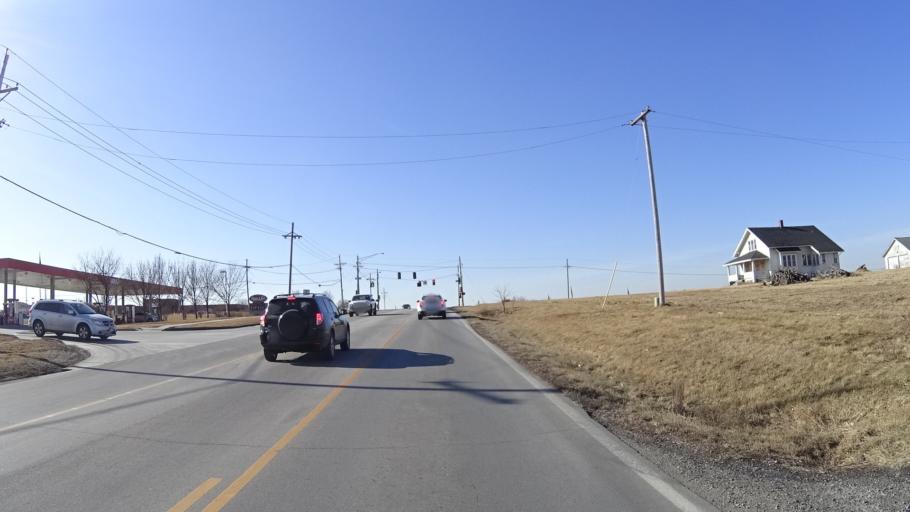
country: US
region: Nebraska
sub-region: Douglas County
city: Bennington
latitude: 41.3067
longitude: -96.1181
